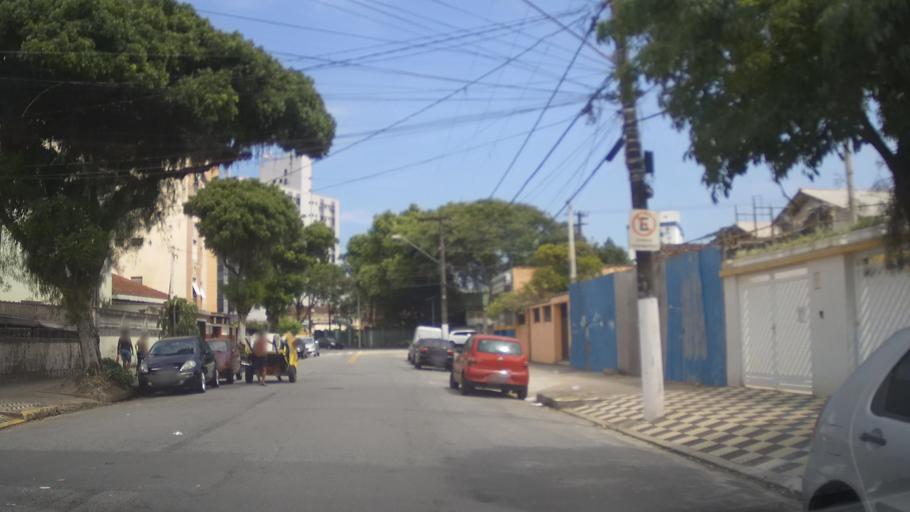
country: BR
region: Sao Paulo
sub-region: Santos
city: Santos
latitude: -23.9642
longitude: -46.3106
